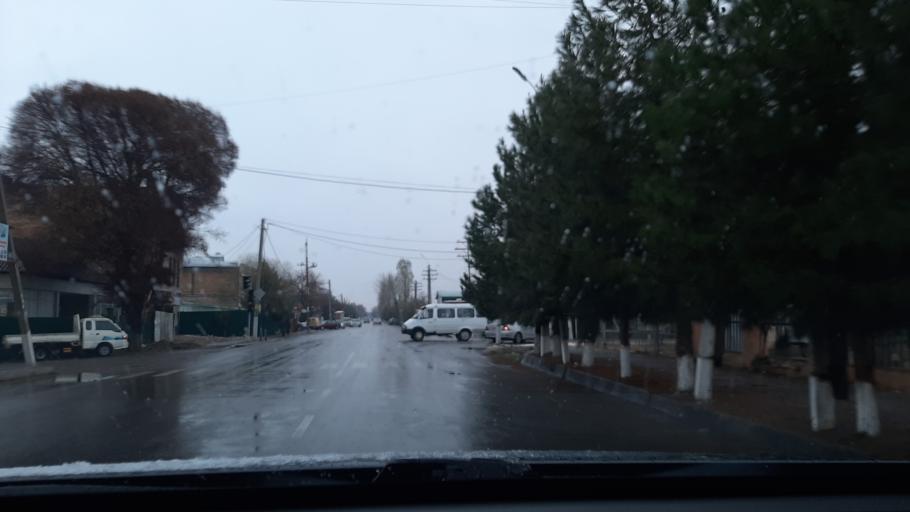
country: TJ
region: Viloyati Sughd
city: Khujand
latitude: 40.2680
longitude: 69.6218
